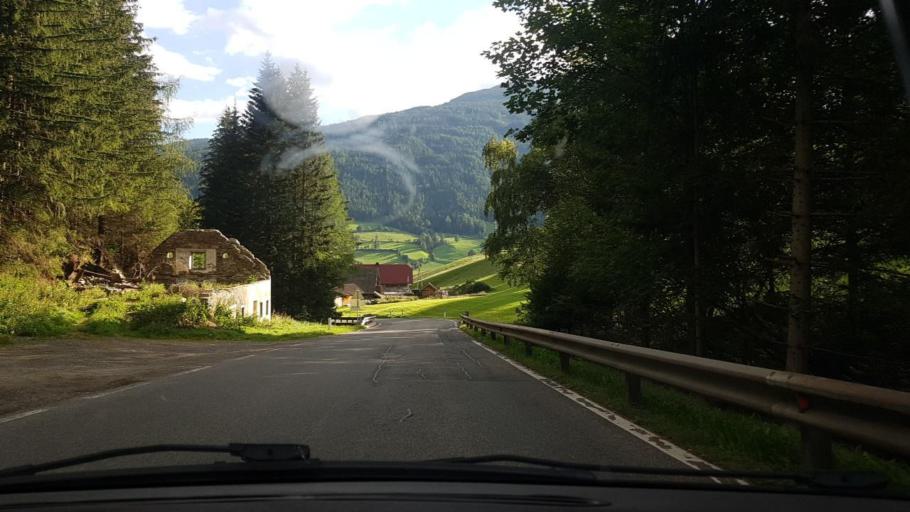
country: AT
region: Salzburg
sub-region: Politischer Bezirk Tamsweg
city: Sankt Michael im Lungau
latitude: 47.0352
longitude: 13.6053
